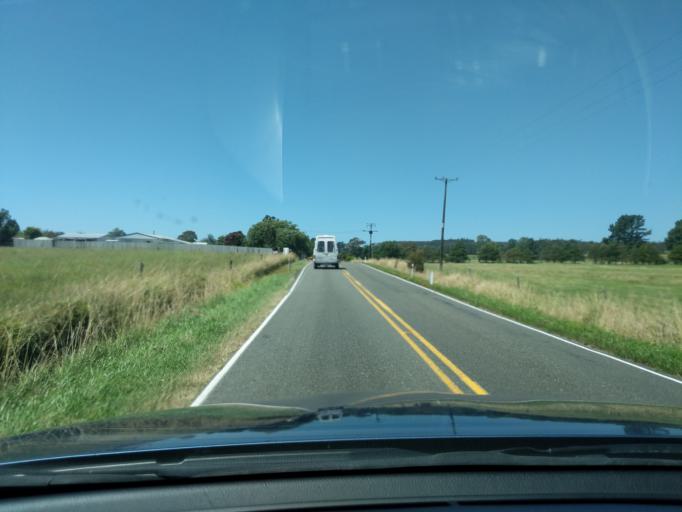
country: NZ
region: Tasman
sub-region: Tasman District
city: Takaka
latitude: -40.6857
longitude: 172.6546
